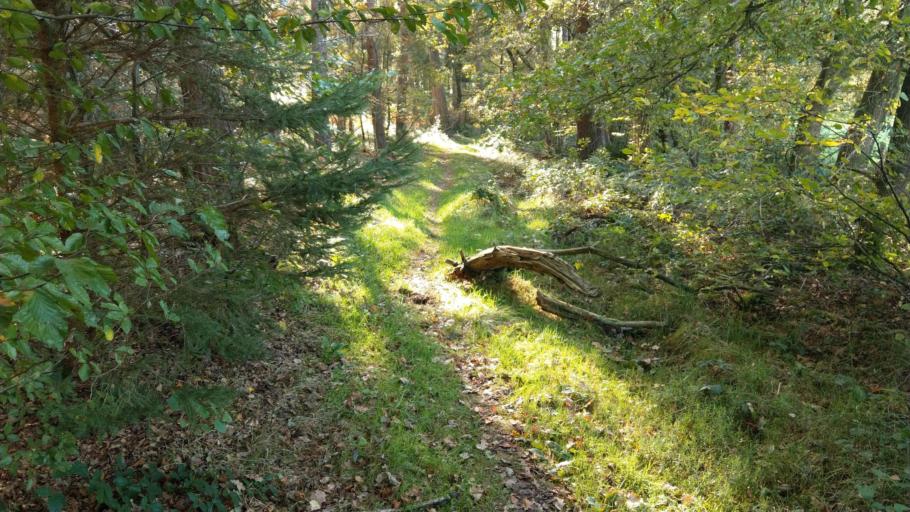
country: BE
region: Wallonia
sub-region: Province de Liege
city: Raeren
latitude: 50.6942
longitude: 6.1248
